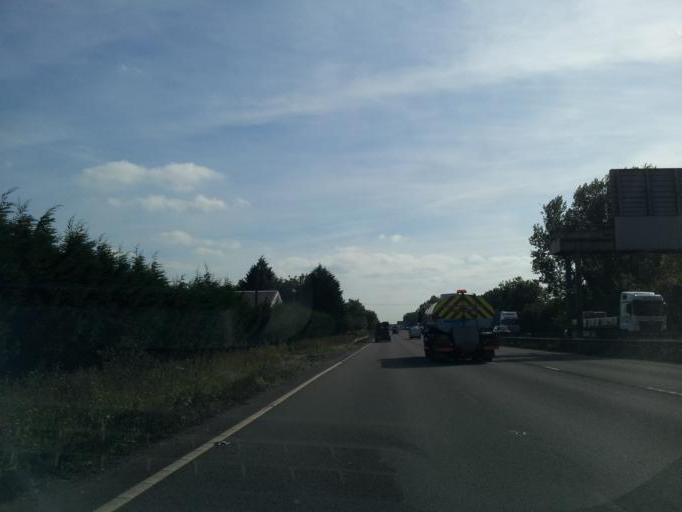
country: GB
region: England
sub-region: Cambridgeshire
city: Girton
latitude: 52.2546
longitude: 0.0299
